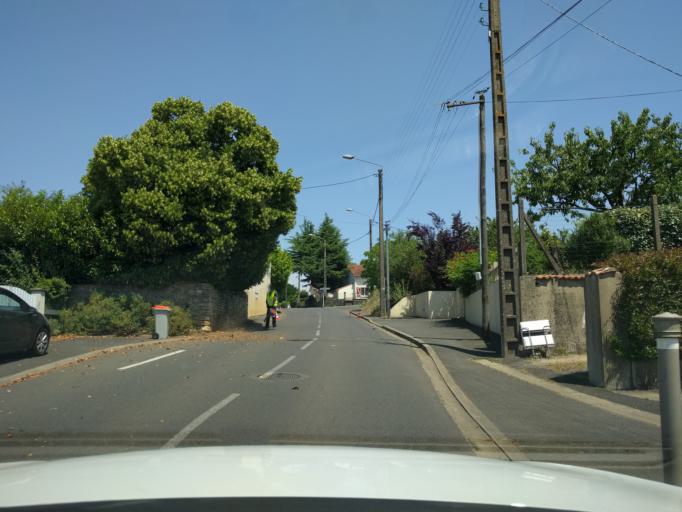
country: FR
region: Poitou-Charentes
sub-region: Departement des Deux-Sevres
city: Niort
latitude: 46.3434
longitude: -0.4631
